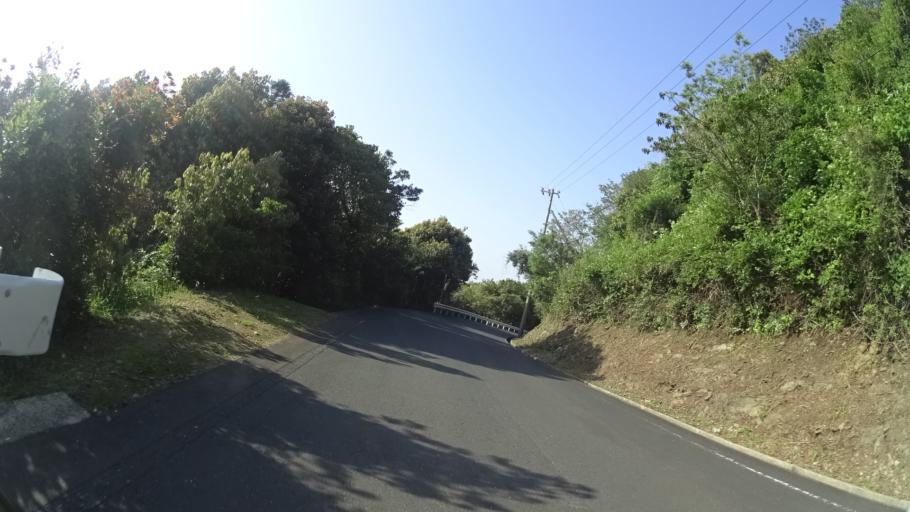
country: JP
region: Ehime
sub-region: Nishiuwa-gun
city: Ikata-cho
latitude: 33.3710
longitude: 132.0572
